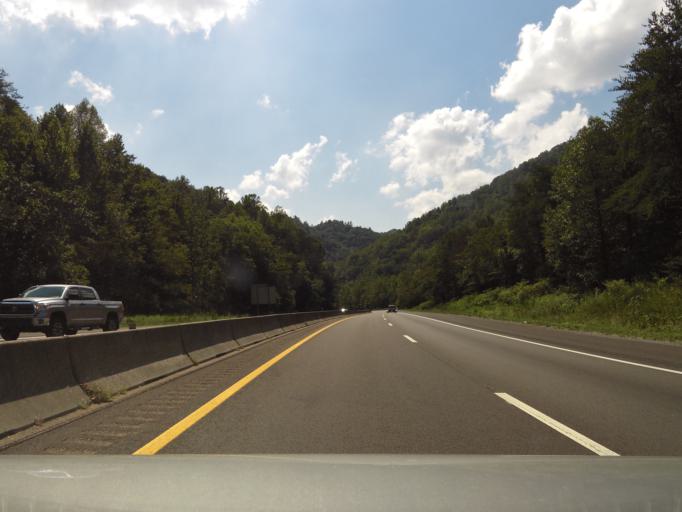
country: US
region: Tennessee
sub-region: Cocke County
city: Newport
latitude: 35.8003
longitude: -83.1313
